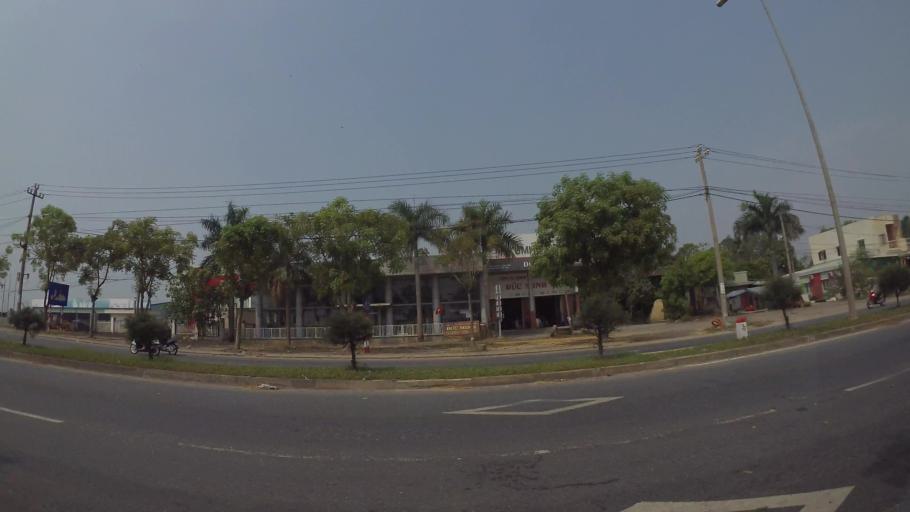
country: VN
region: Da Nang
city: Cam Le
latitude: 15.9747
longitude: 108.2085
